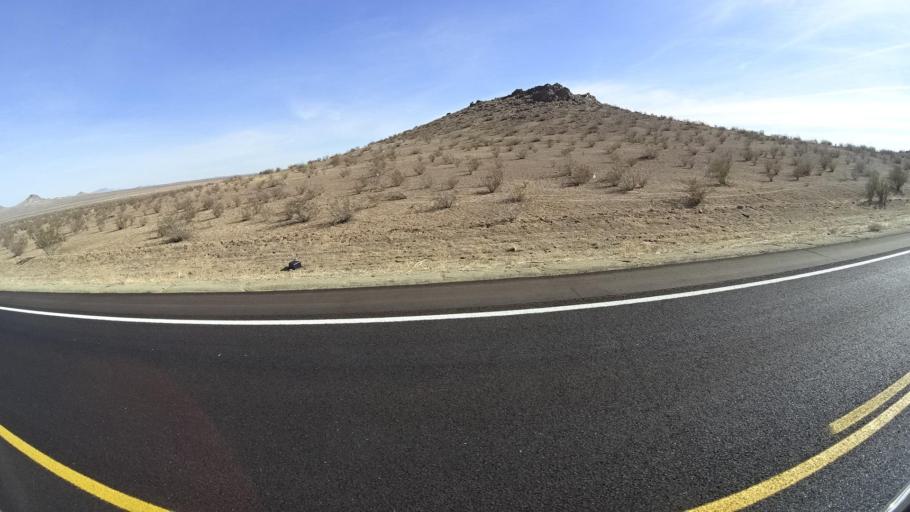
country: US
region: California
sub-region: Kern County
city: California City
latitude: 35.0636
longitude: -117.9174
